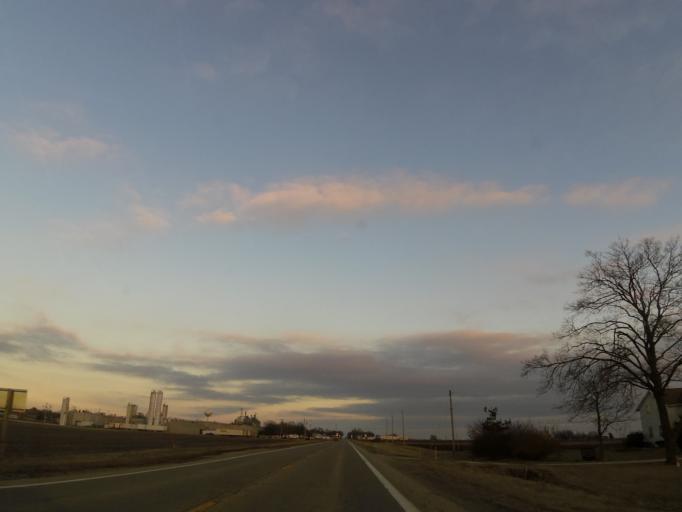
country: US
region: Illinois
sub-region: McLean County
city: Gridley
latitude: 40.7395
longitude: -88.8934
